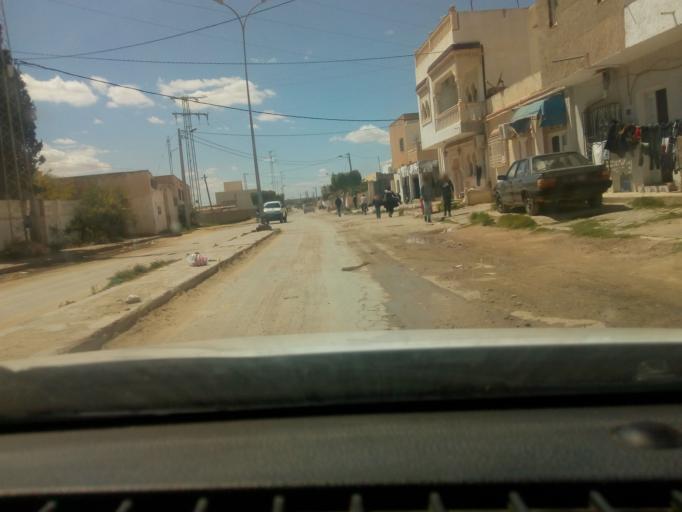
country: TN
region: Safaqis
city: Sfax
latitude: 34.7379
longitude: 10.5255
